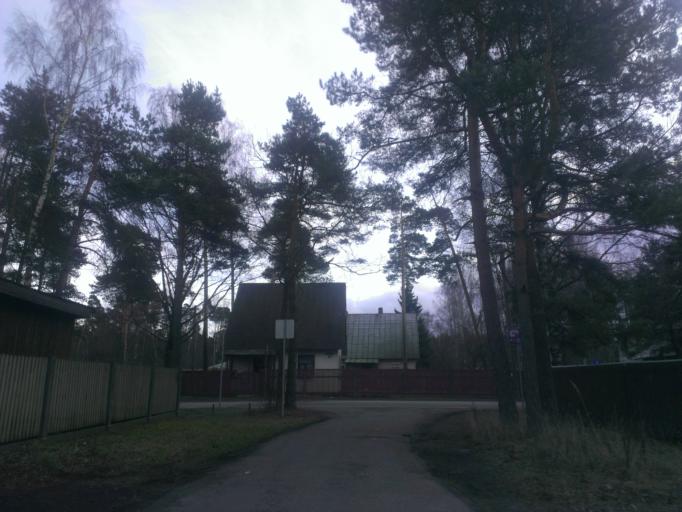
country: LV
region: Riga
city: Bolderaja
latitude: 57.0488
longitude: 24.0978
